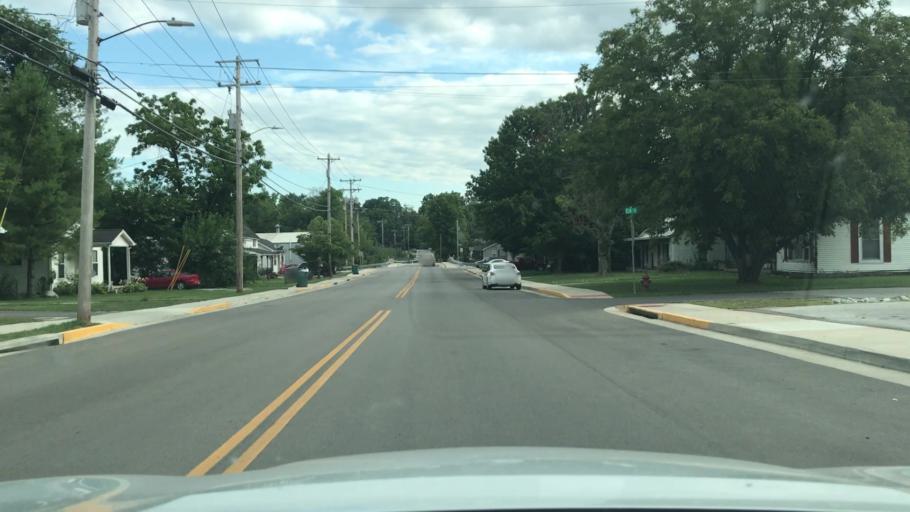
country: US
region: Kentucky
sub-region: Todd County
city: Elkton
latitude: 36.8115
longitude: -87.1535
